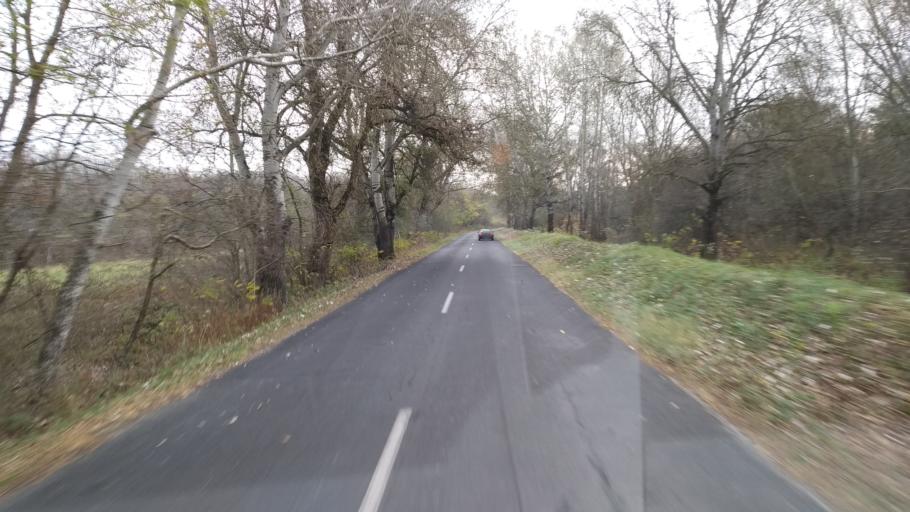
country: HU
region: Pest
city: Dunabogdany
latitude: 47.7952
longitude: 19.0663
